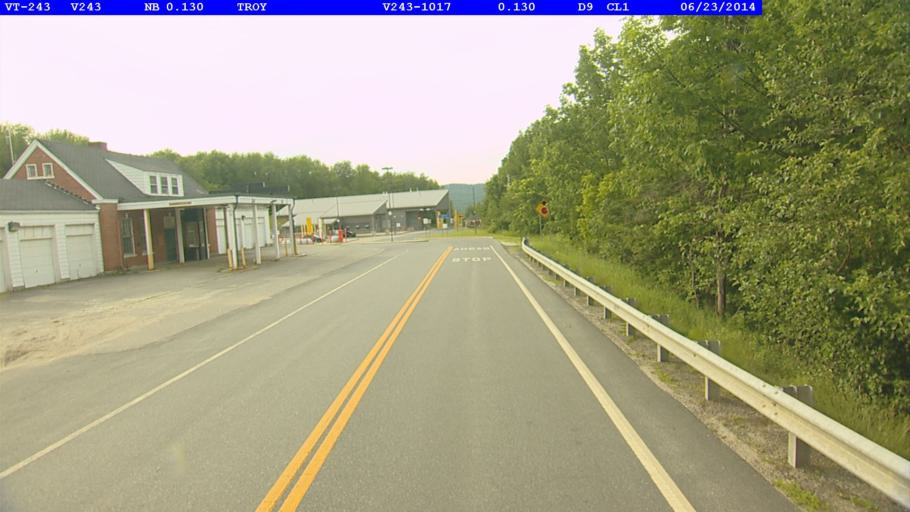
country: US
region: Vermont
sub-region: Orleans County
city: Newport
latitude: 45.0054
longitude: -72.4149
